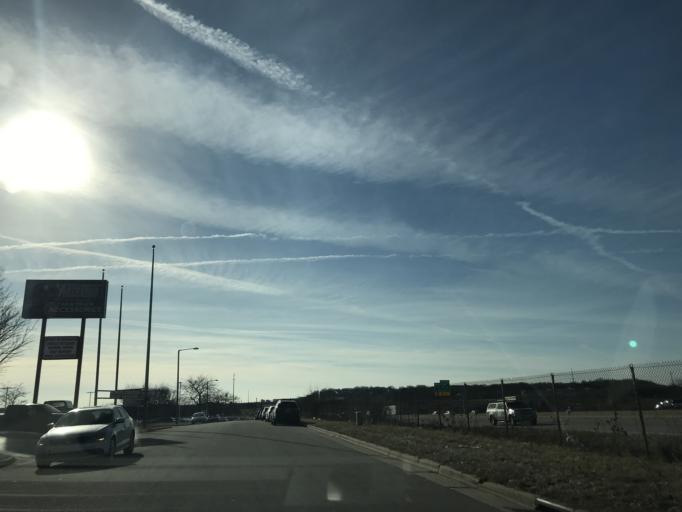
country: US
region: Wisconsin
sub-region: Dane County
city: Sun Prairie
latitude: 43.1417
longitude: -89.2899
